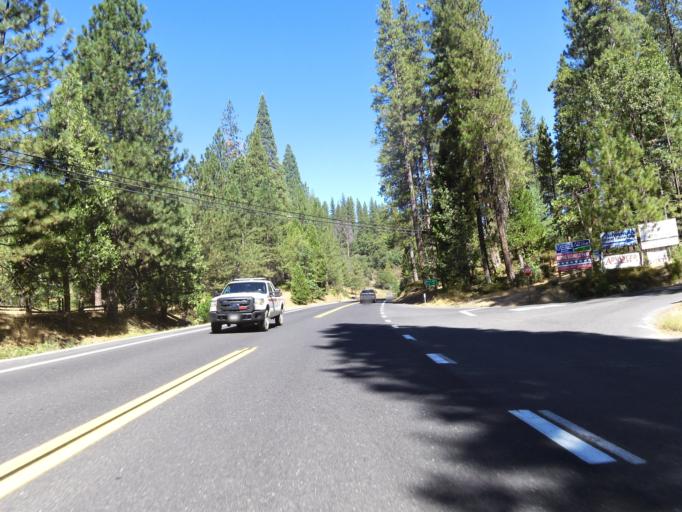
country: US
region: California
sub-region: Calaveras County
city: Forest Meadows
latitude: 38.1957
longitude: -120.3654
